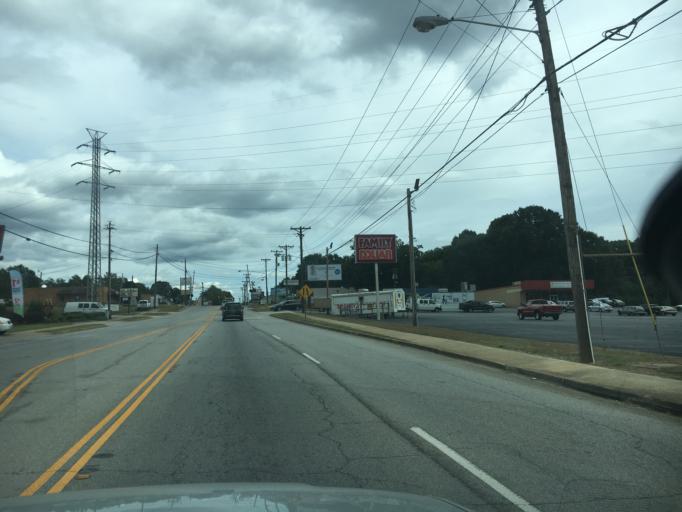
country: US
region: South Carolina
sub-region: Laurens County
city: Laurens
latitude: 34.5048
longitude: -82.0091
